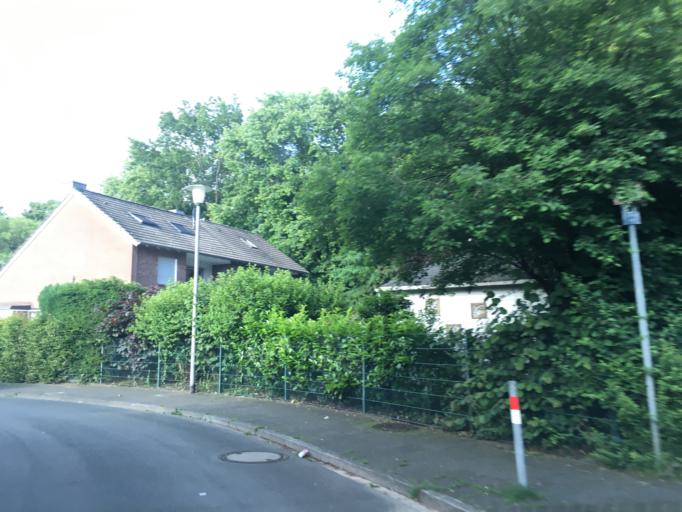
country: DE
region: North Rhine-Westphalia
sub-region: Regierungsbezirk Munster
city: Muenster
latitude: 51.9947
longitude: 7.6465
